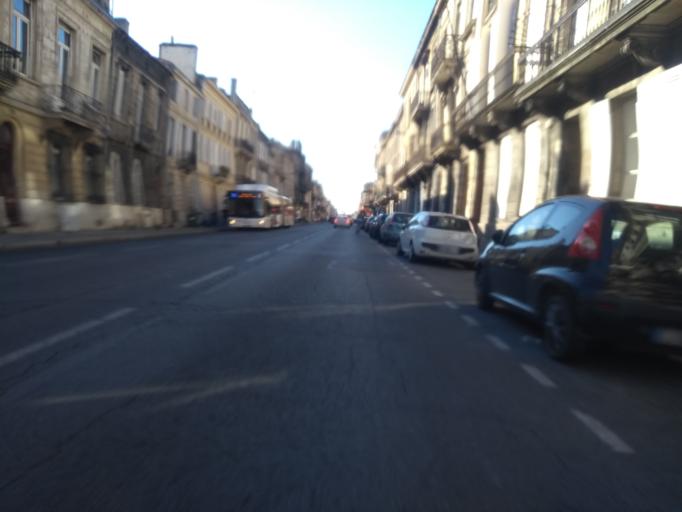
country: FR
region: Aquitaine
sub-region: Departement de la Gironde
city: Bordeaux
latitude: 44.8316
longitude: -0.5759
